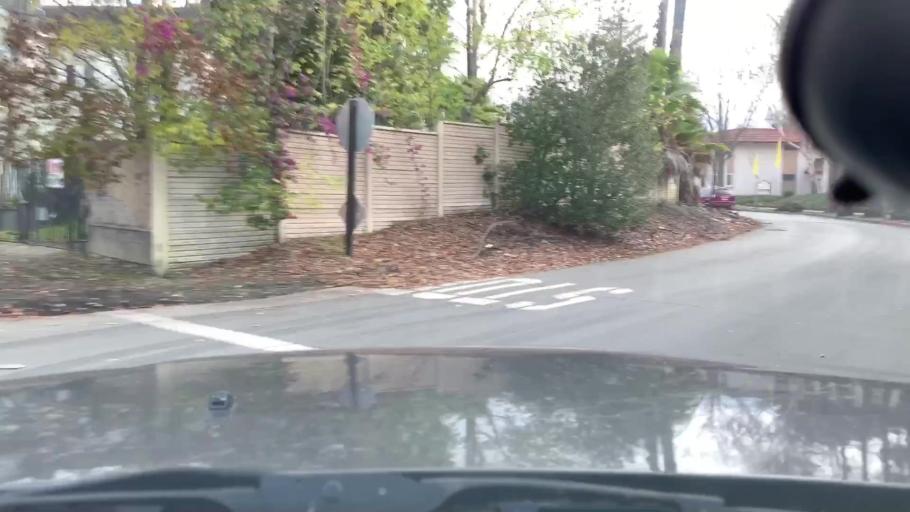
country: US
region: California
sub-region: Santa Clara County
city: Campbell
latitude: 37.3045
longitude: -121.9759
